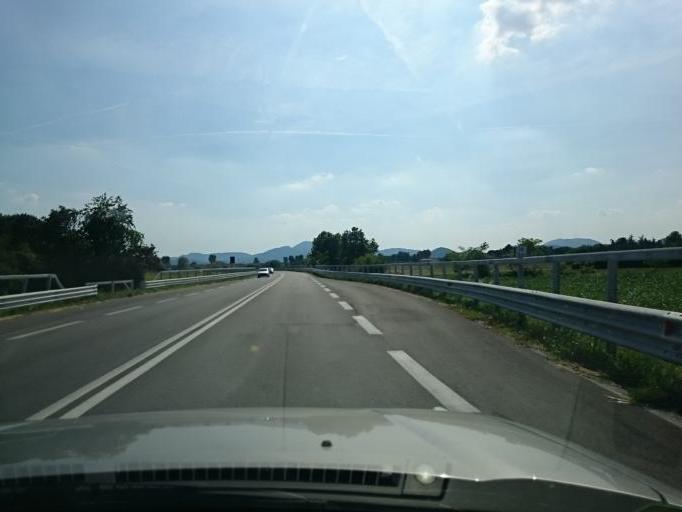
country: IT
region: Veneto
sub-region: Provincia di Padova
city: Abano Terme
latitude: 45.3647
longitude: 11.8126
